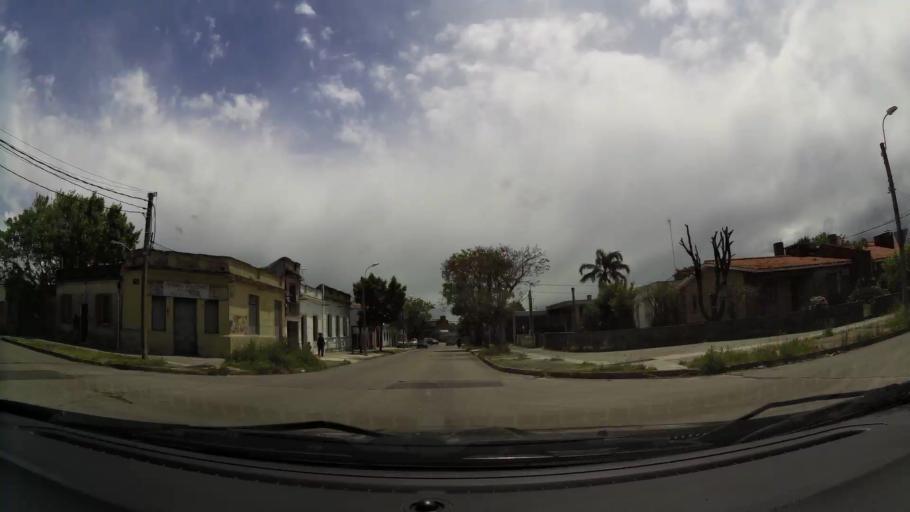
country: UY
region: Montevideo
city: Montevideo
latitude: -34.8744
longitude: -56.1264
